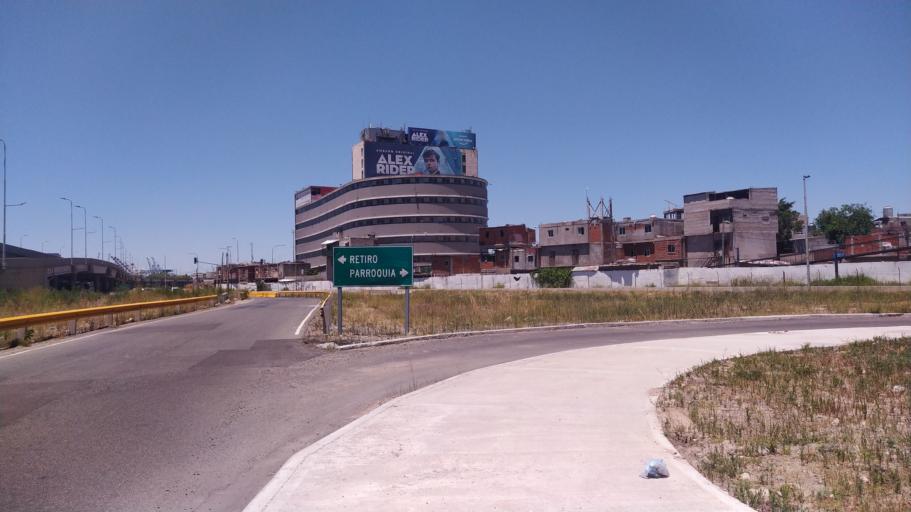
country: AR
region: Buenos Aires F.D.
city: Retiro
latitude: -34.5777
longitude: -58.3884
